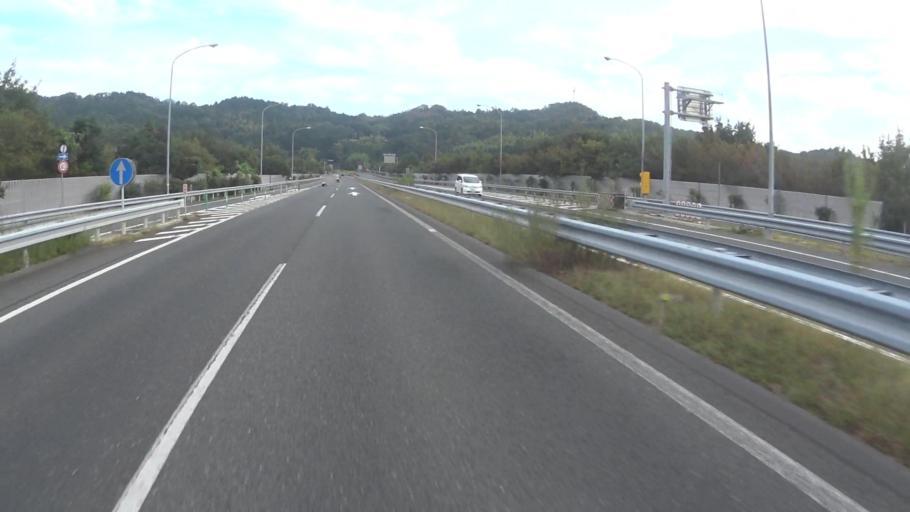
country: JP
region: Kyoto
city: Kameoka
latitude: 35.0526
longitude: 135.5347
